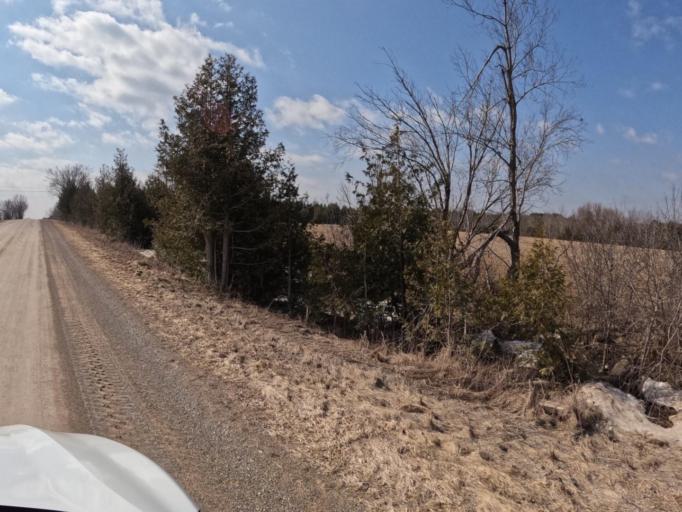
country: CA
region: Ontario
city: Orangeville
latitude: 43.9170
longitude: -80.2547
